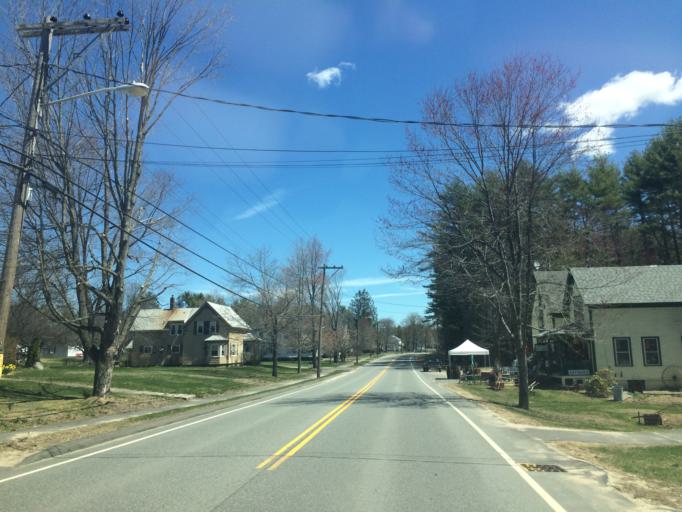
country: US
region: Maine
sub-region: Oxford County
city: Porter
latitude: 43.8067
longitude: -70.8811
